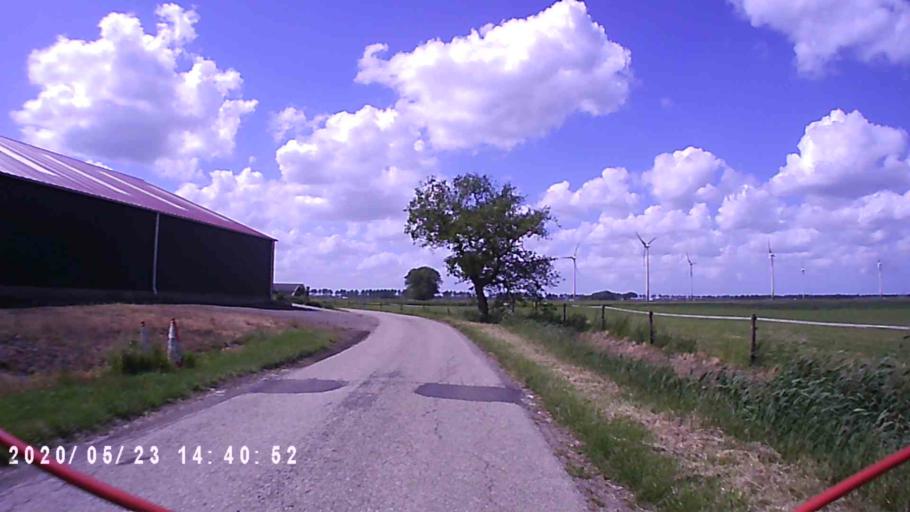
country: NL
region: Groningen
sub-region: Gemeente Delfzijl
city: Delfzijl
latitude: 53.2724
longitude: 6.9672
